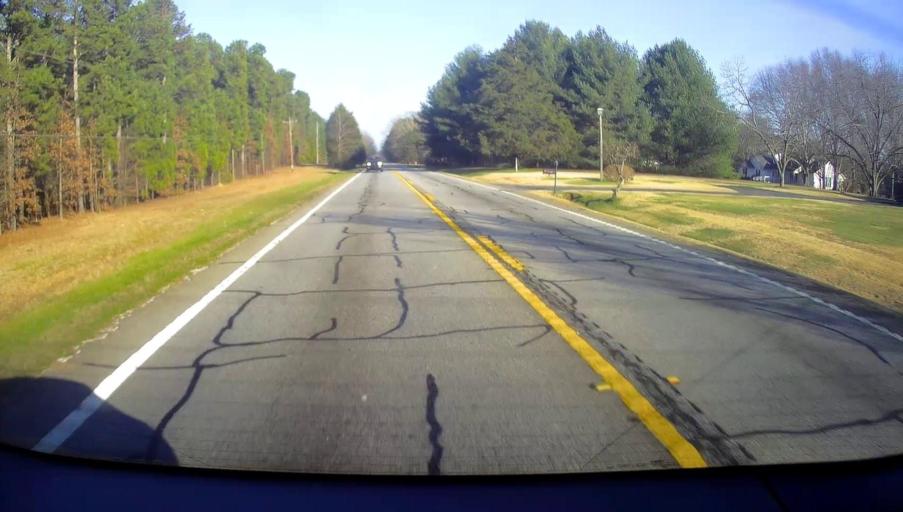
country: US
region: Georgia
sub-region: Henry County
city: Hampton
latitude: 33.4191
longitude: -84.2580
